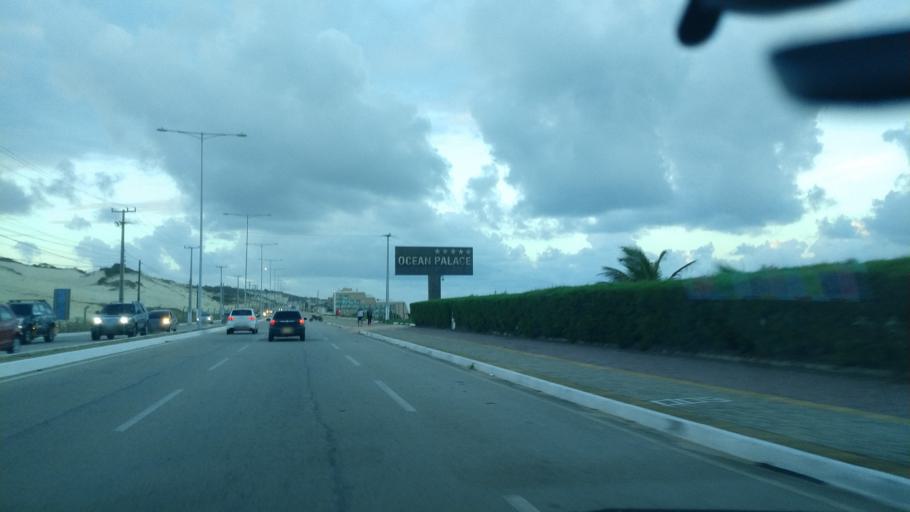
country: BR
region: Rio Grande do Norte
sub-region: Natal
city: Natal
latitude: -5.8599
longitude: -35.1813
